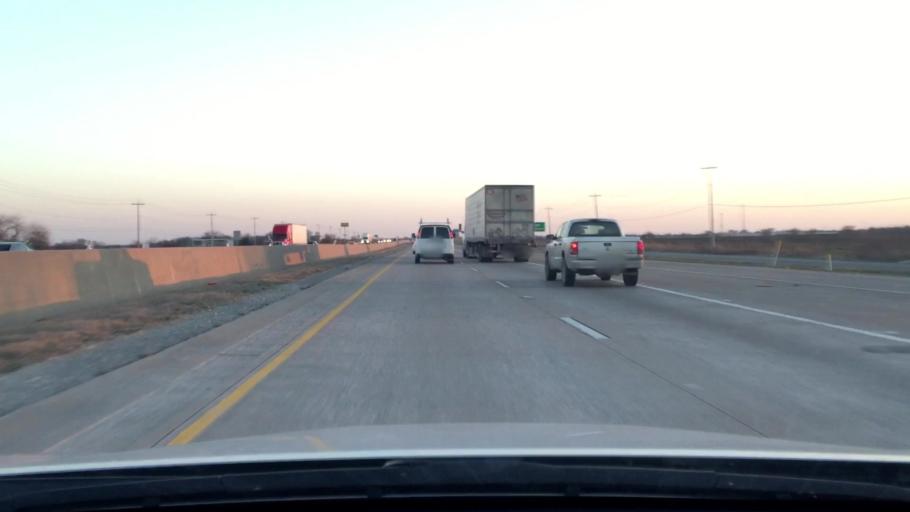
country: US
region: Texas
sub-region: Denton County
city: Sanger
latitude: 33.3903
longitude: -97.1770
